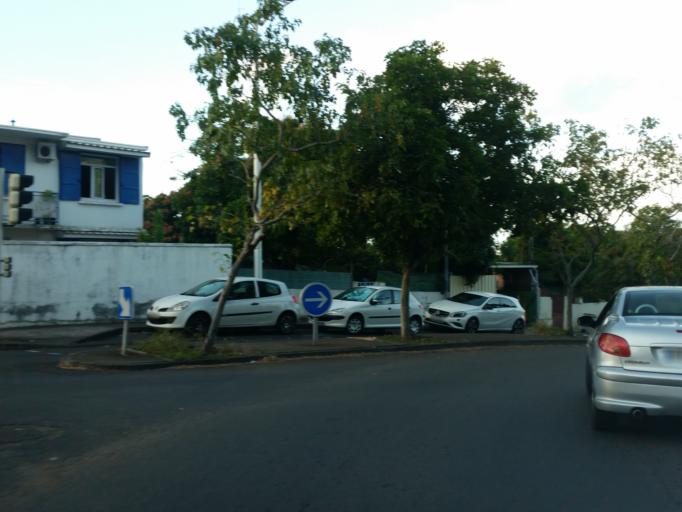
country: RE
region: Reunion
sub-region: Reunion
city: Saint-Denis
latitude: -20.8895
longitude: 55.4452
